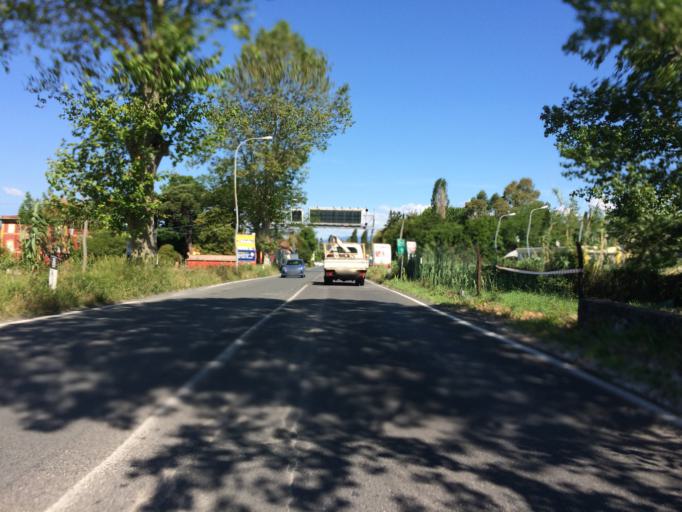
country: IT
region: Tuscany
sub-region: Provincia di Massa-Carrara
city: Borghetto-Melara
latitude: 44.0975
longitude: 9.9859
